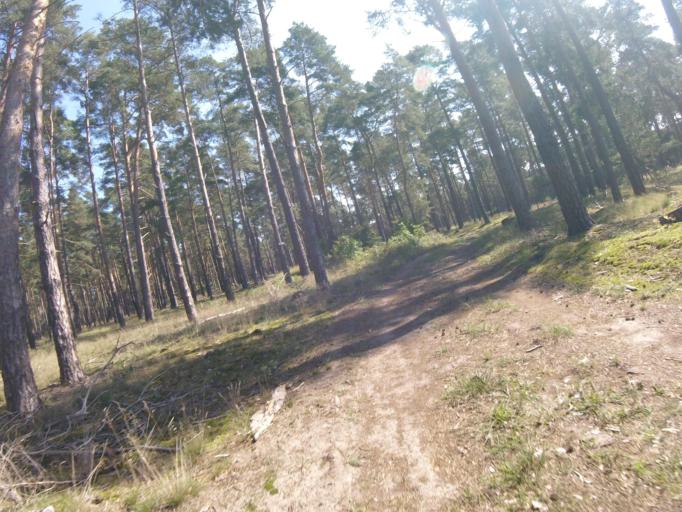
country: DE
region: Brandenburg
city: Mittenwalde
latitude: 52.2206
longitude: 13.5886
